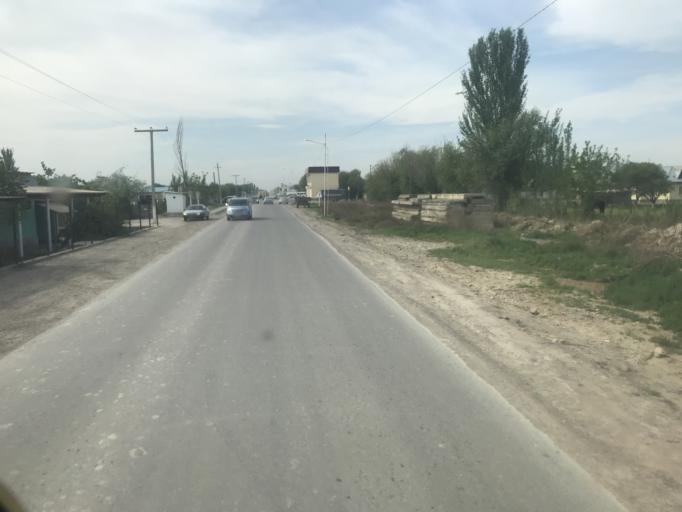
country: KZ
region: Ongtustik Qazaqstan
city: Asykata
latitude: 41.0063
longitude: 68.2151
